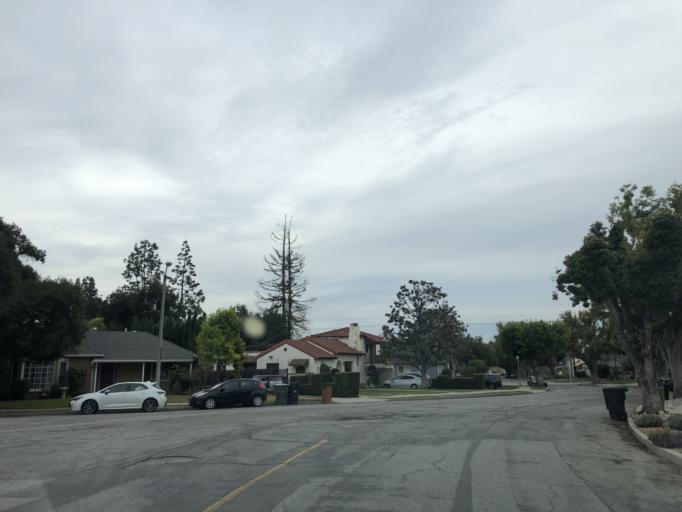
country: US
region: California
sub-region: Los Angeles County
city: San Gabriel
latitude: 34.1073
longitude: -118.1056
